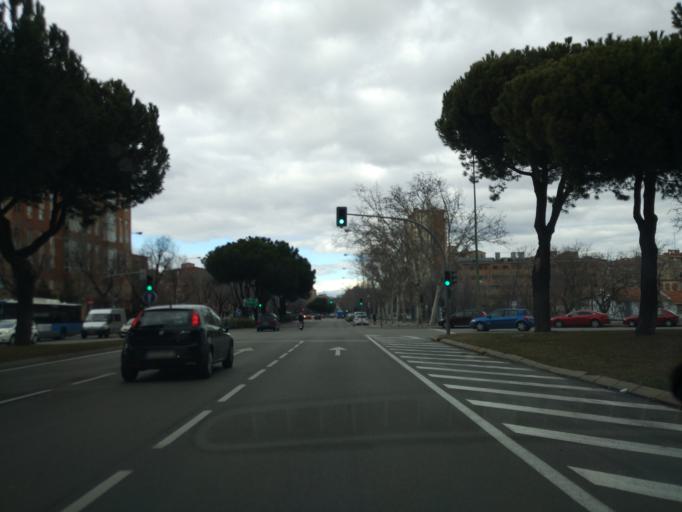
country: ES
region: Madrid
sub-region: Provincia de Madrid
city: San Blas
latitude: 40.4245
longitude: -3.6282
